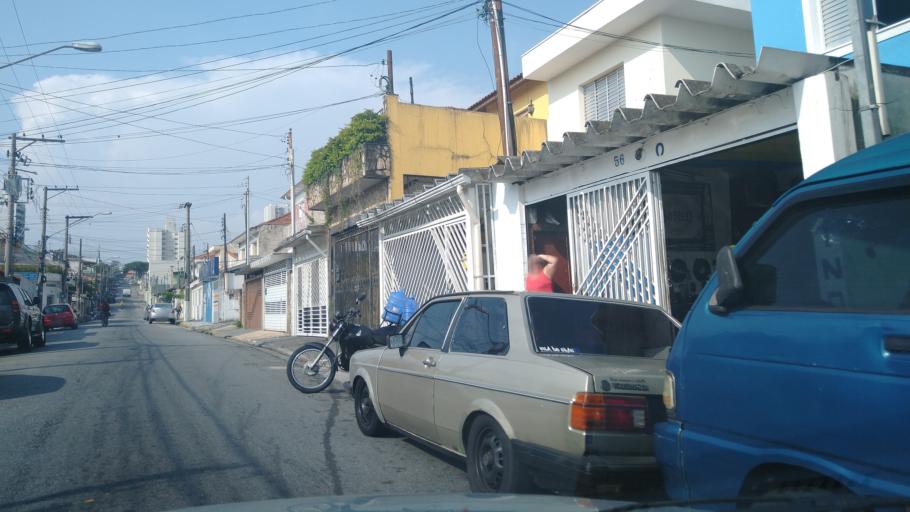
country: BR
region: Sao Paulo
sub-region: Sao Paulo
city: Sao Paulo
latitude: -23.5033
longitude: -46.5974
